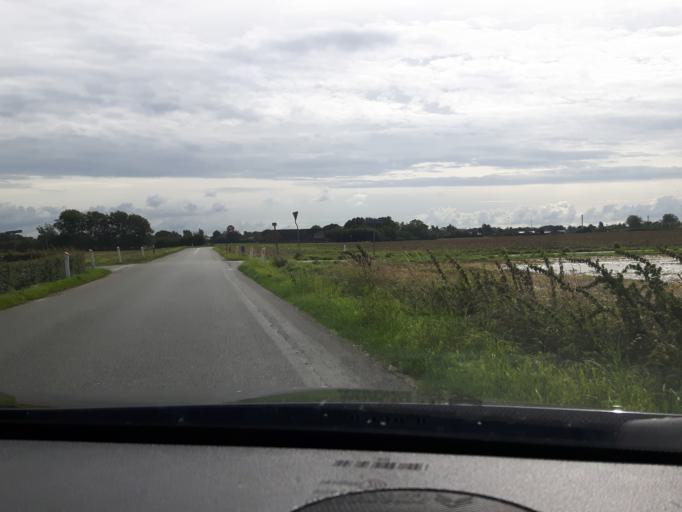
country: DK
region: South Denmark
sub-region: Fredericia Kommune
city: Fredericia
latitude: 55.6023
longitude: 9.7697
